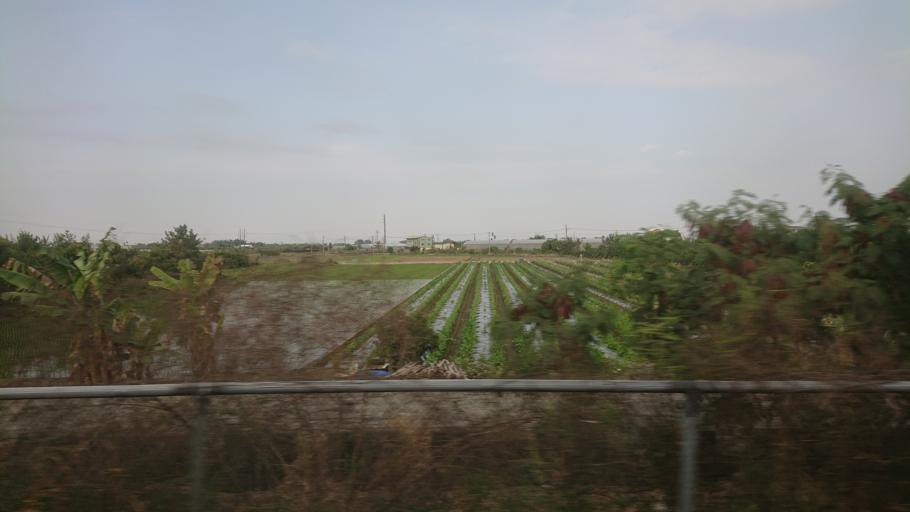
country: TW
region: Taiwan
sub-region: Yunlin
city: Douliu
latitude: 23.7362
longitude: 120.5846
